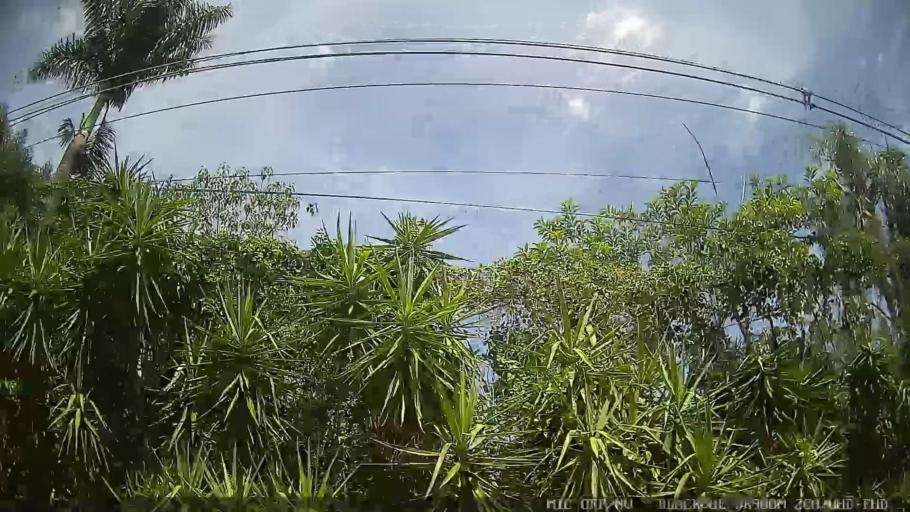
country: BR
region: Sao Paulo
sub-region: Jaguariuna
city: Jaguariuna
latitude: -22.6195
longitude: -47.0616
